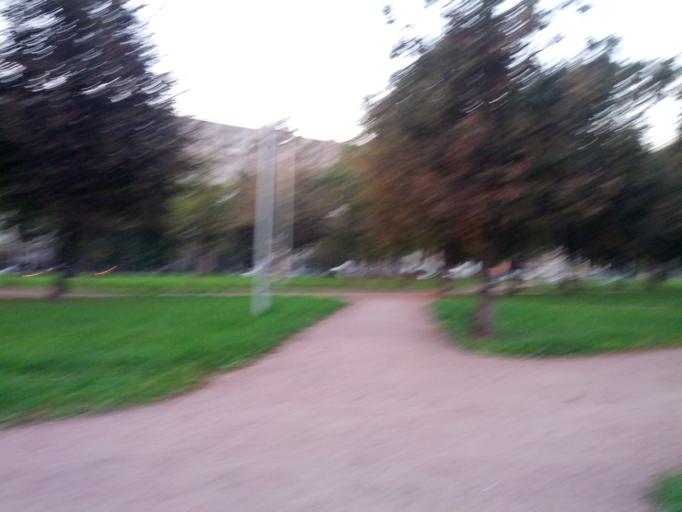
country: RU
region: St.-Petersburg
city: Obukhovo
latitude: 59.8962
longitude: 30.4687
